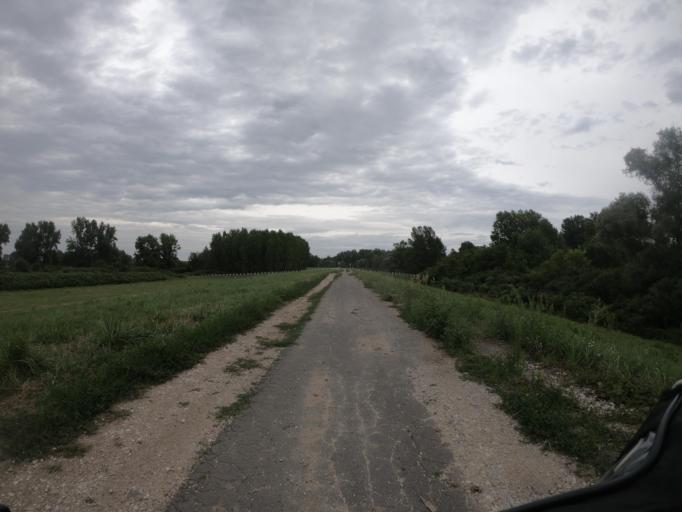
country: HU
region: Hajdu-Bihar
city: Tiszacsege
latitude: 47.7039
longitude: 20.9278
